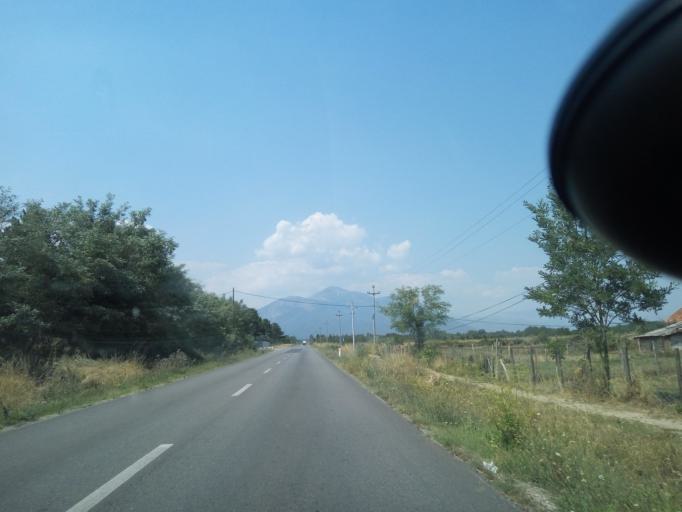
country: XK
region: Gjakova
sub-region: Komuna e Decanit
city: Prilep
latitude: 42.4788
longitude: 20.3353
